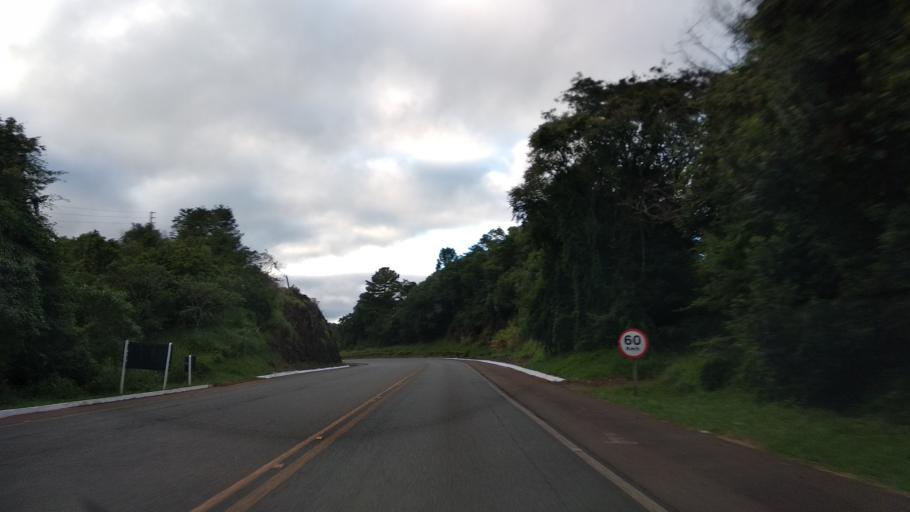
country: BR
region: Santa Catarina
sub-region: Campos Novos
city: Campos Novos
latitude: -27.5336
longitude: -50.8734
